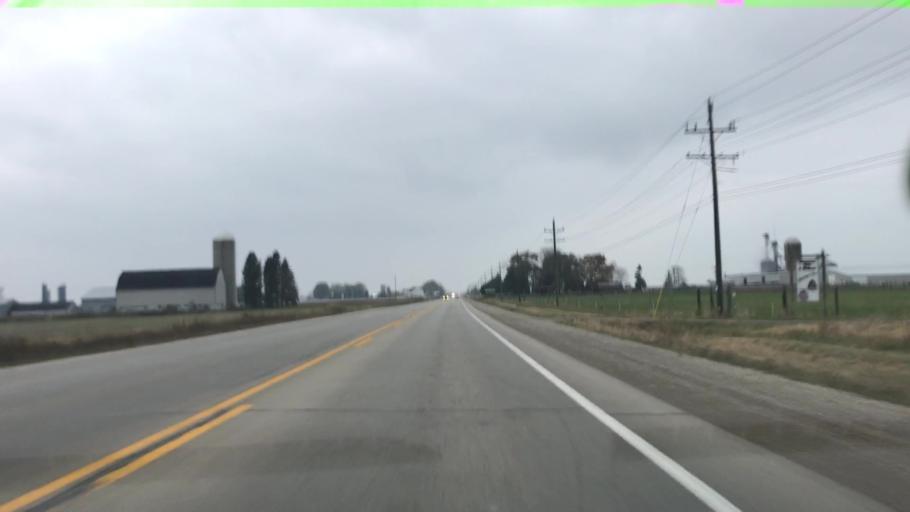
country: US
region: Wisconsin
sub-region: Outagamie County
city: Seymour
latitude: 44.5002
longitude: -88.2948
